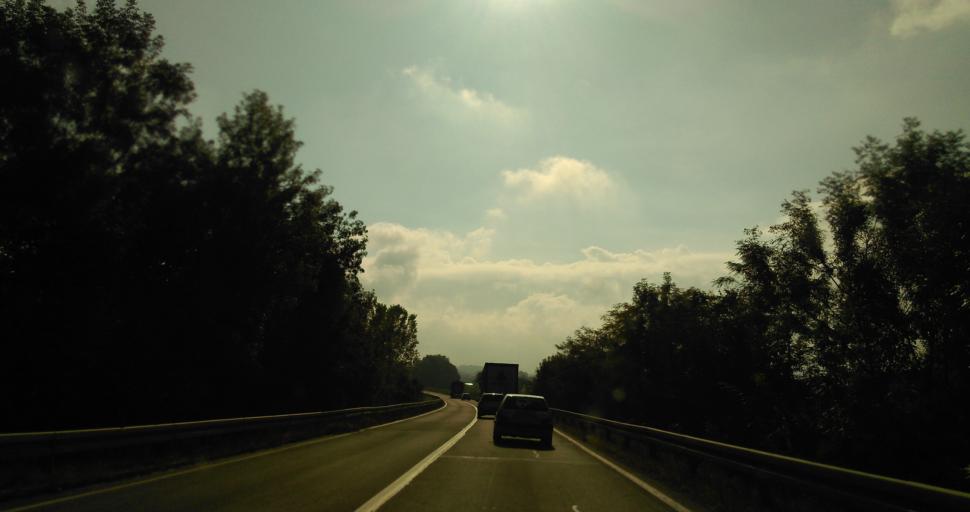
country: RS
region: Central Serbia
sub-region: Kolubarski Okrug
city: Lajkovac
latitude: 44.3457
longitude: 20.1980
